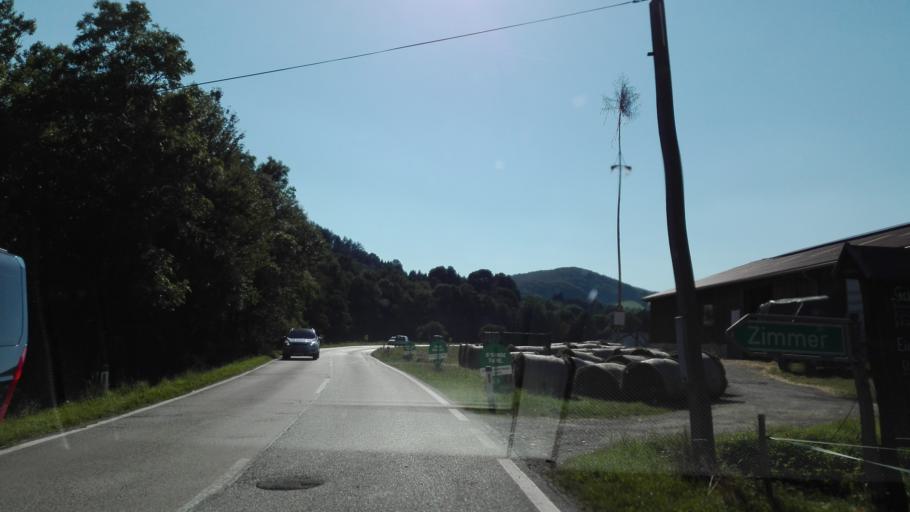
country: AT
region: Lower Austria
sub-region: Politischer Bezirk Baden
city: Klausen-Leopoldsdorf
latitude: 48.0829
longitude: 16.0309
